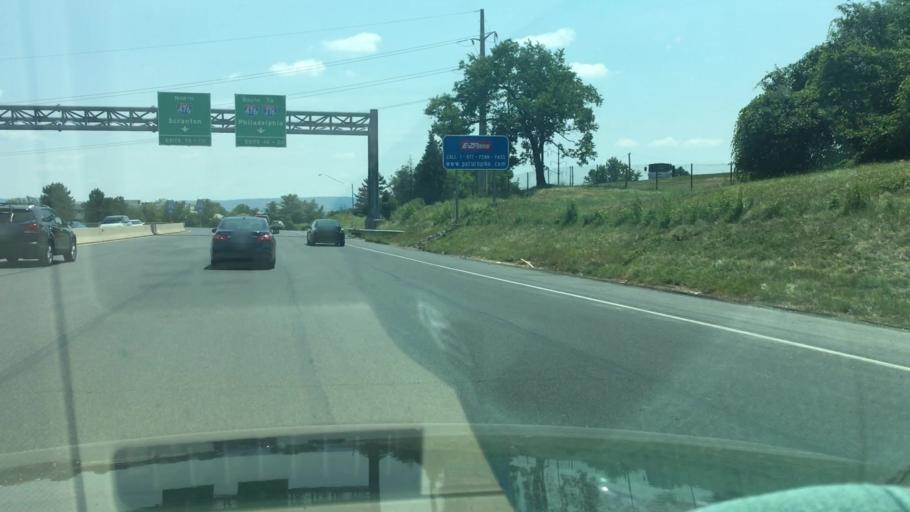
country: US
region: Pennsylvania
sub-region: Lehigh County
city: Wescosville
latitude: 40.5925
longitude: -75.5687
